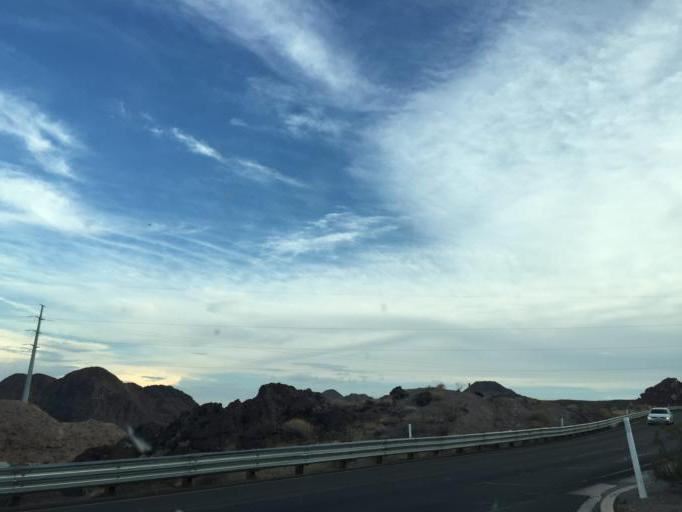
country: US
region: Nevada
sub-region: Clark County
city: Boulder City
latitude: 36.0146
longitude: -114.7600
